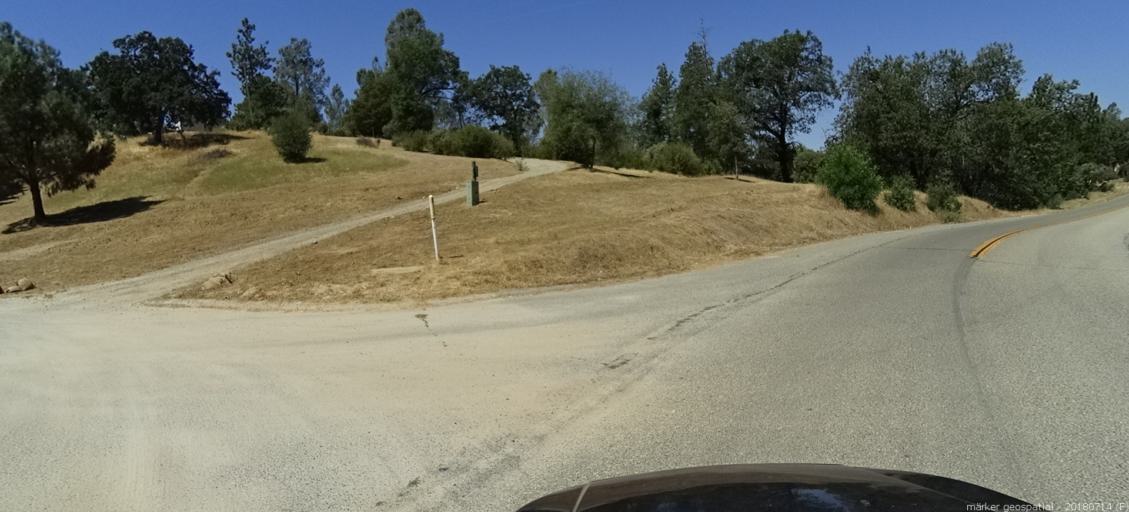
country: US
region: California
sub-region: Madera County
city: Oakhurst
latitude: 37.3667
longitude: -119.6575
